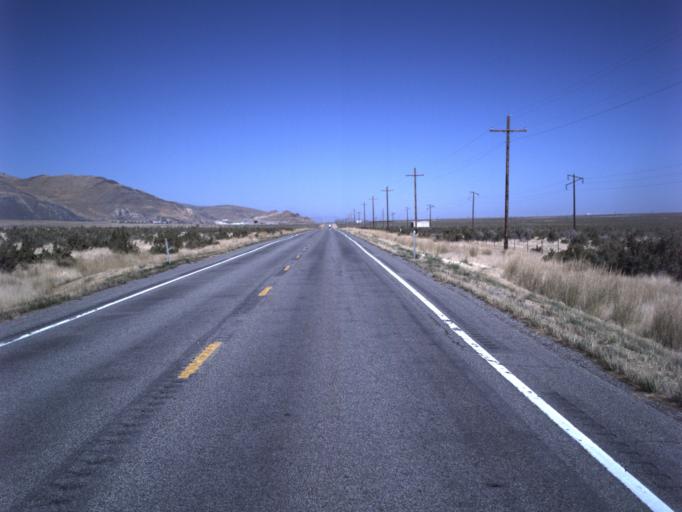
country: US
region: Utah
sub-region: Tooele County
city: Grantsville
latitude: 40.6575
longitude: -112.5369
